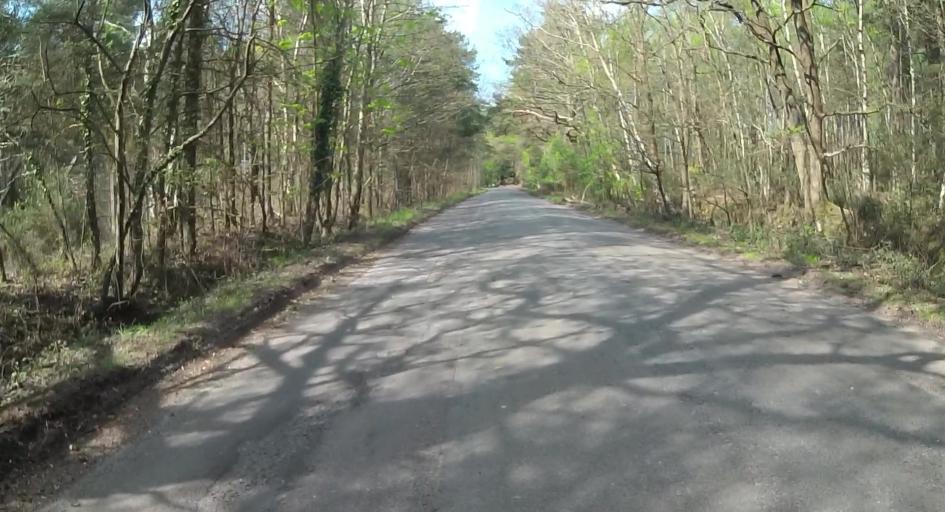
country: GB
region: England
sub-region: Hampshire
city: Tadley
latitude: 51.3703
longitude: -1.1219
